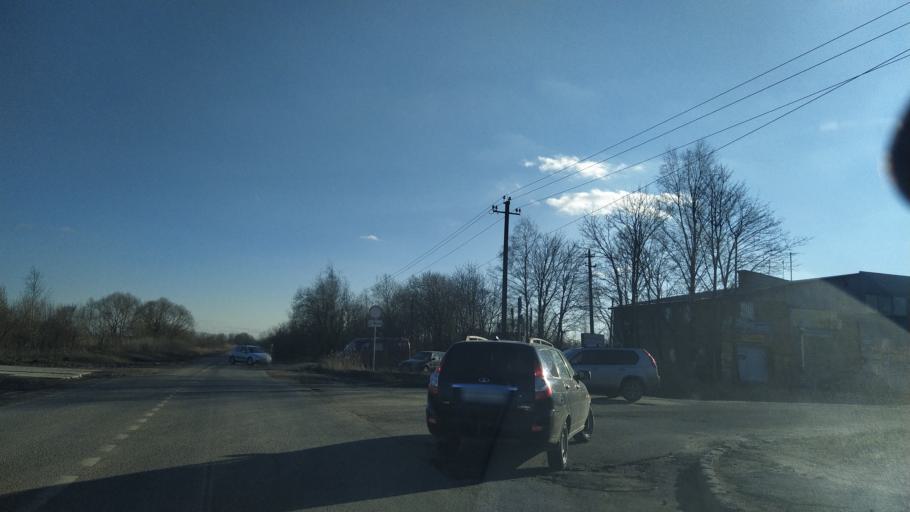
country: RU
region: St.-Petersburg
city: Pushkin
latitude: 59.6955
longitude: 30.3957
